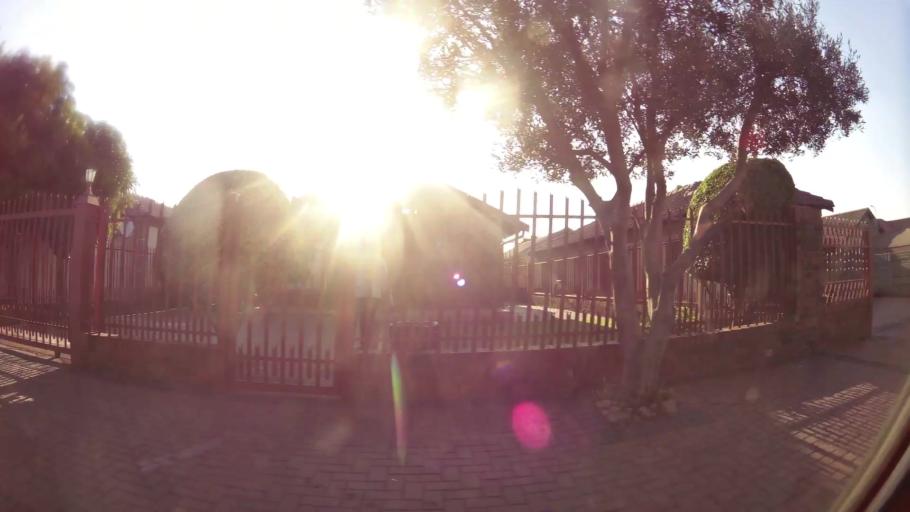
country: ZA
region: North-West
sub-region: Bojanala Platinum District Municipality
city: Rustenburg
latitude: -25.6483
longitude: 27.2236
